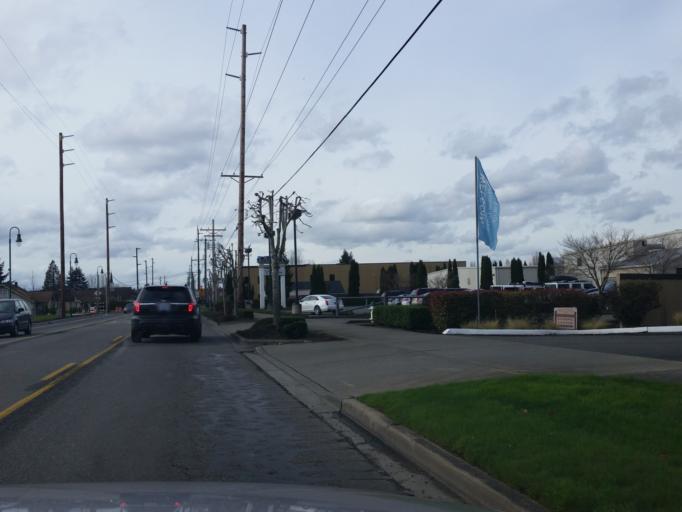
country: US
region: Washington
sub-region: Pierce County
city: Fife
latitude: 47.2390
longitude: -122.3426
